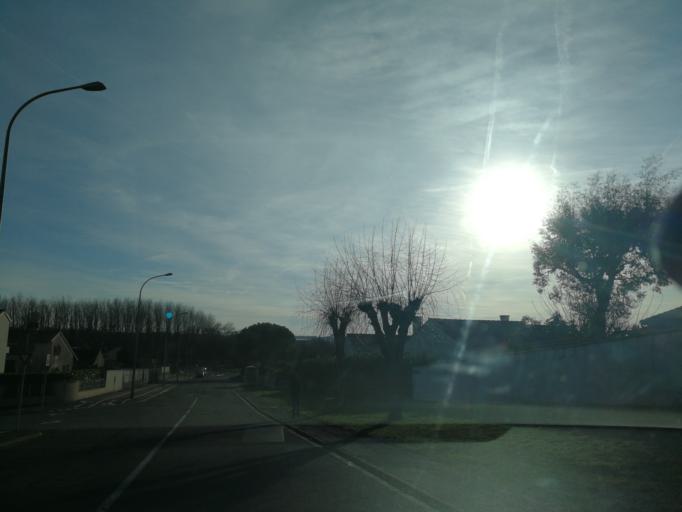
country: FR
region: Midi-Pyrenees
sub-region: Departement de la Haute-Garonne
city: Saint-Jean
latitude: 43.6501
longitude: 1.4967
